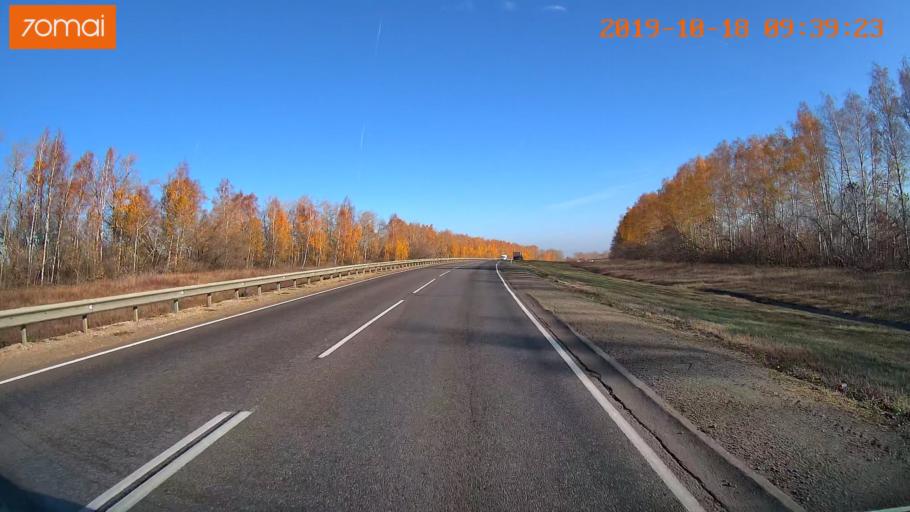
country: RU
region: Tula
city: Yefremov
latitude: 53.2526
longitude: 38.1350
